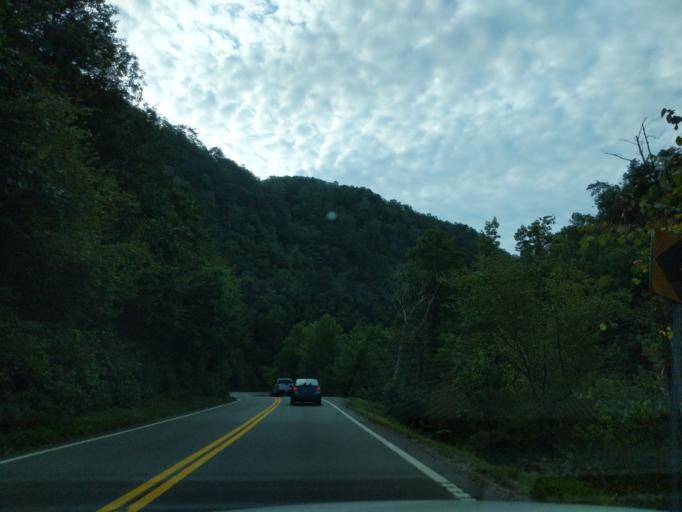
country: US
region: Tennessee
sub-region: Polk County
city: Benton
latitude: 35.0914
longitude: -84.5303
